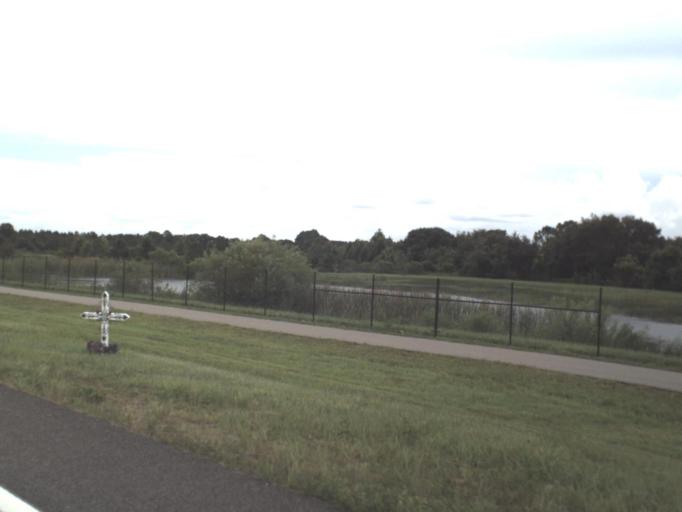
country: US
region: Florida
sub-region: Hillsborough County
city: Pebble Creek
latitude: 28.1866
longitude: -82.3480
